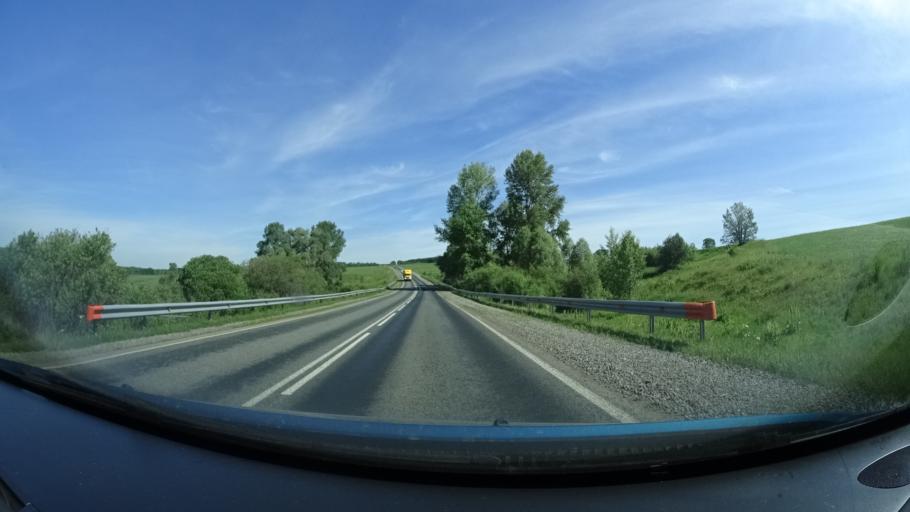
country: RU
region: Bashkortostan
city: Blagoveshchensk
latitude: 55.1226
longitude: 55.8417
